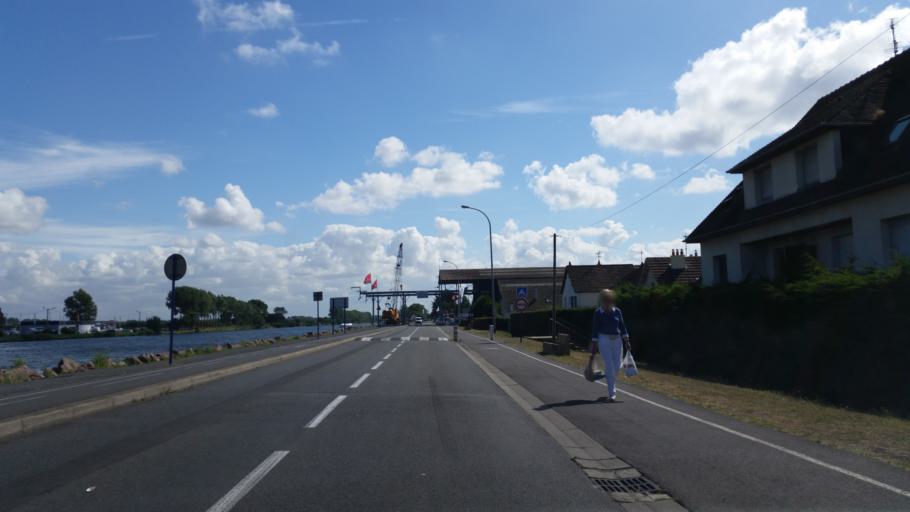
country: FR
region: Lower Normandy
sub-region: Departement du Calvados
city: Ouistreham
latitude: 49.2759
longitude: -0.2510
